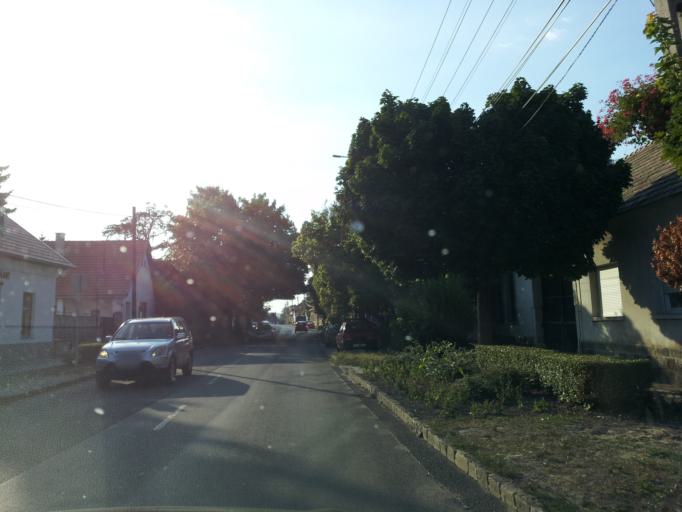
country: HU
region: Pest
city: Dunabogdany
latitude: 47.7951
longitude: 19.0336
